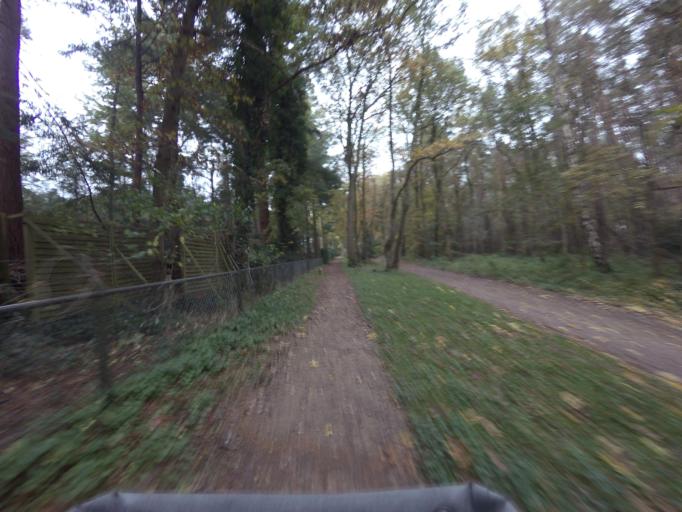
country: NL
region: North Holland
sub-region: Gemeente Hilversum
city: Hilversum
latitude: 52.2081
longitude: 5.1965
